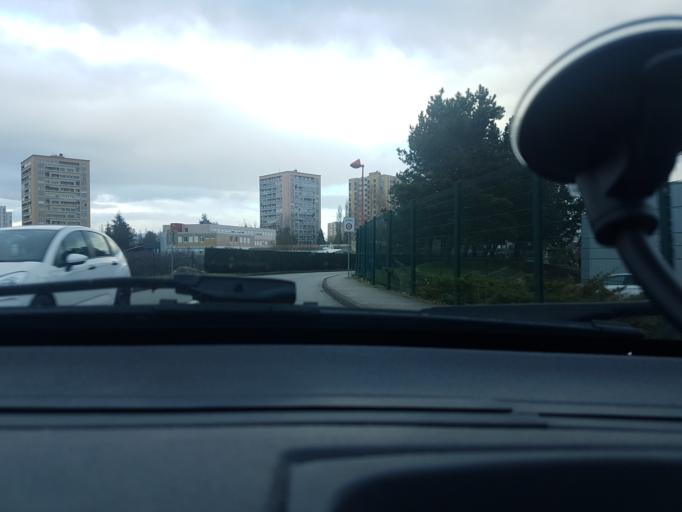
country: FR
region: Franche-Comte
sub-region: Territoire de Belfort
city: Bavilliers
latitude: 47.6282
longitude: 6.8385
